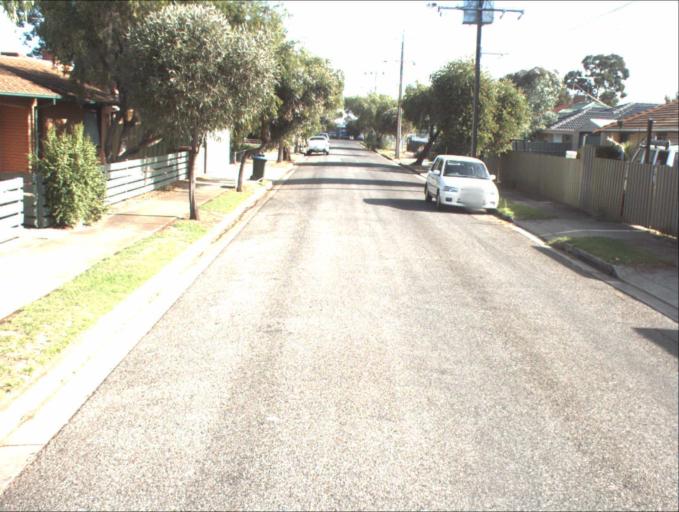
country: AU
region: South Australia
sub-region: Charles Sturt
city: Woodville North
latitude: -34.8655
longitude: 138.5501
